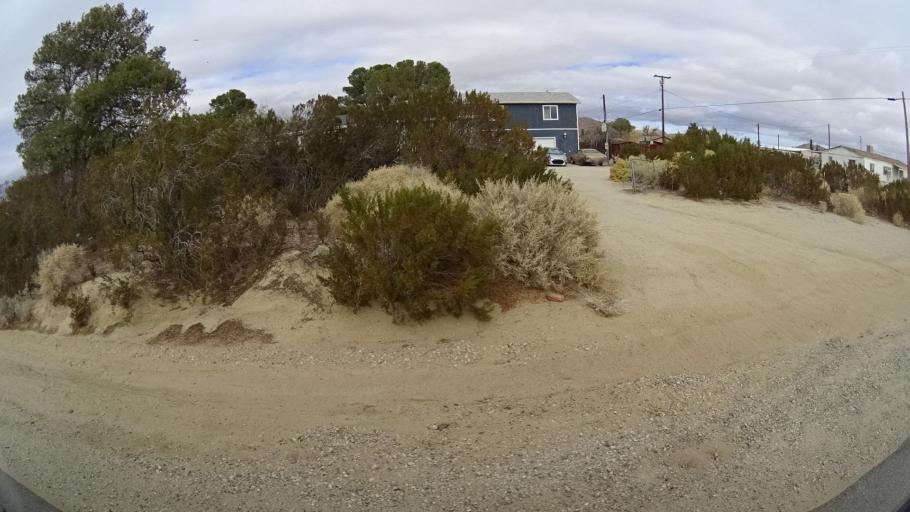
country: US
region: California
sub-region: Kern County
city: Rosamond
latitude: 34.8928
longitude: -118.2395
